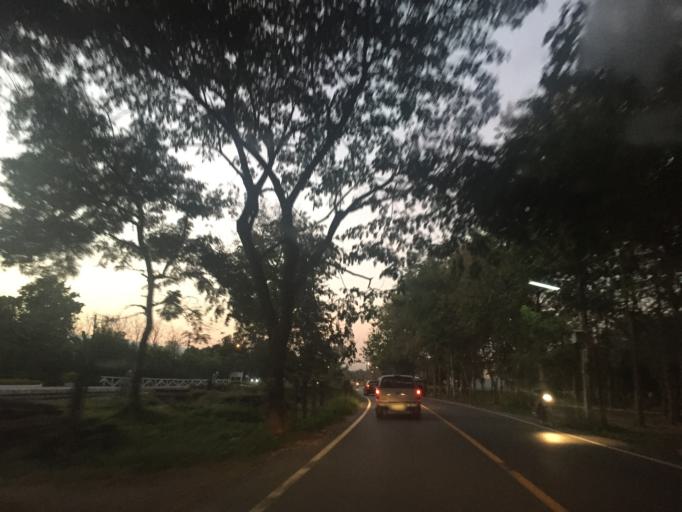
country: TH
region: Chiang Mai
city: Saraphi
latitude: 18.7101
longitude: 99.0421
